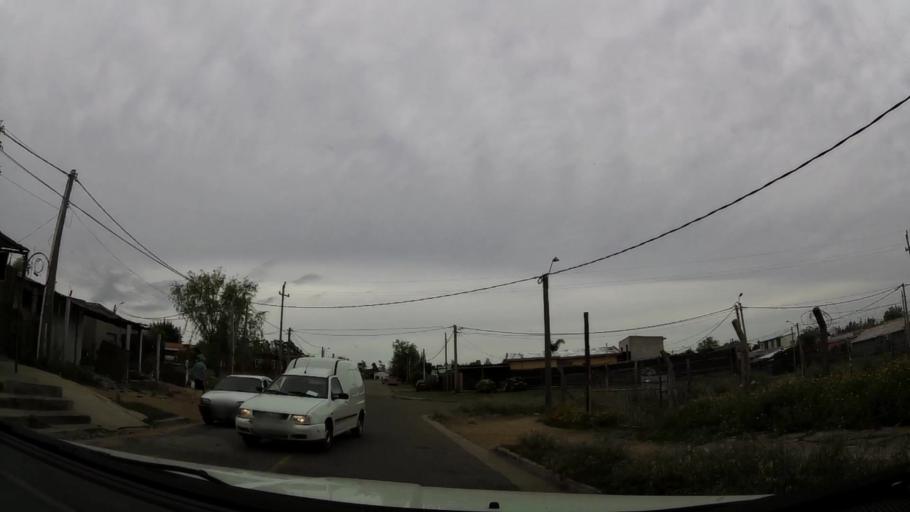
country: UY
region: Maldonado
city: Maldonado
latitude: -34.8791
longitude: -54.9795
